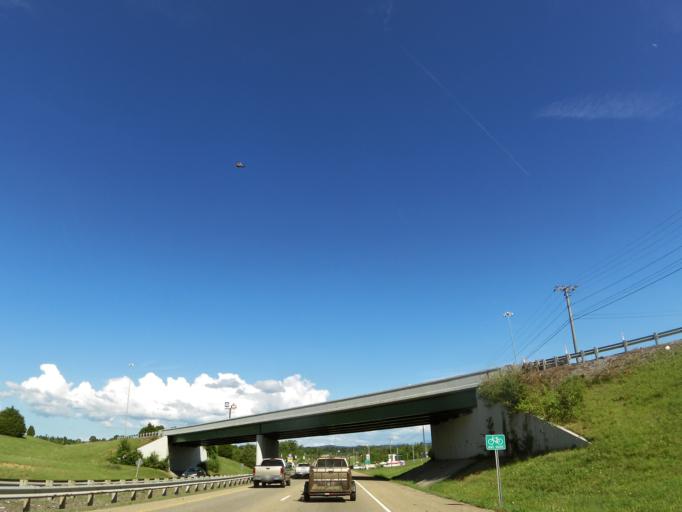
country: US
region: Tennessee
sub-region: Greene County
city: Mosheim
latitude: 36.2244
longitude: -83.0413
